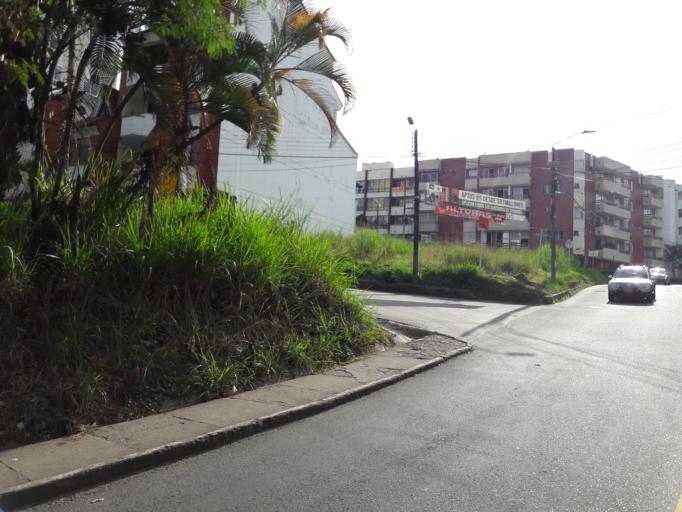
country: CO
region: Tolima
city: Ibague
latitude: 4.4363
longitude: -75.2076
